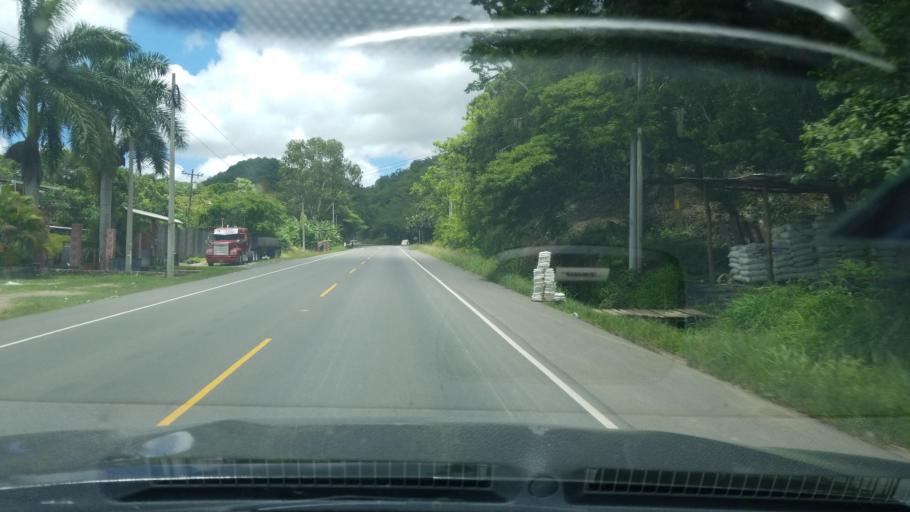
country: HN
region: Francisco Morazan
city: Talanga
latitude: 14.3803
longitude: -87.1364
